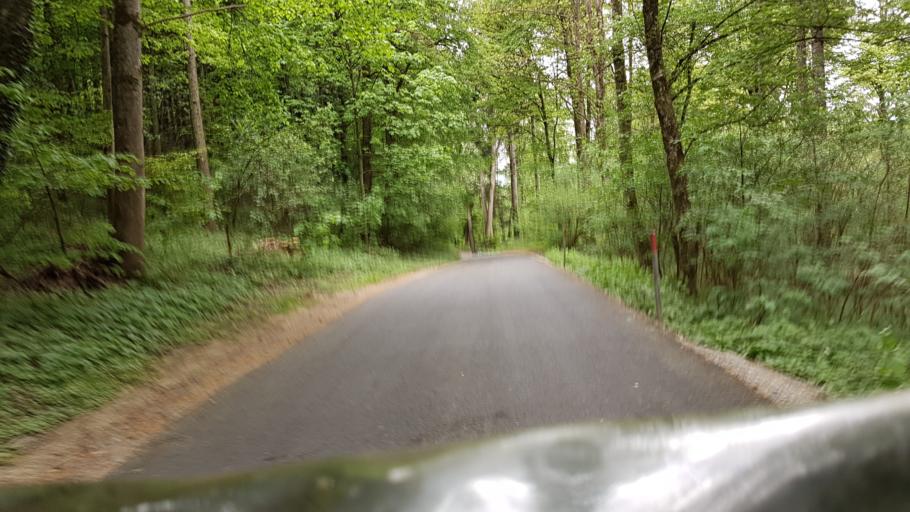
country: CH
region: Bern
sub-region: Bern-Mittelland District
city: Munsingen
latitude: 46.8665
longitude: 7.5446
